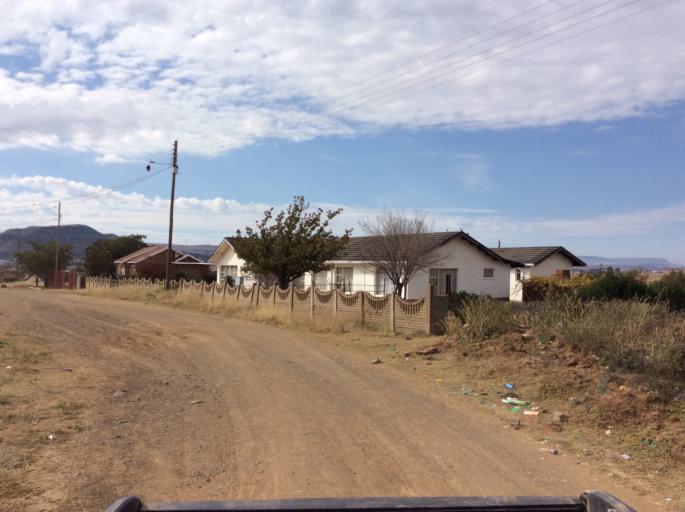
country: LS
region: Mafeteng
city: Mafeteng
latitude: -29.7242
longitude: 27.0099
